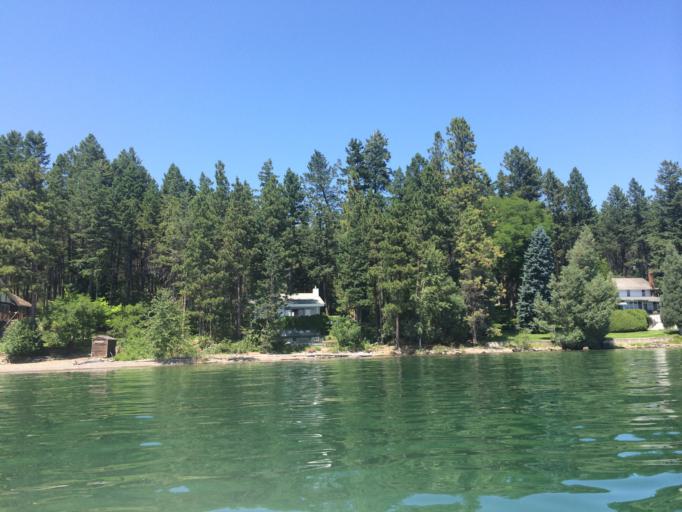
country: US
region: Montana
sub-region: Flathead County
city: Lakeside
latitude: 48.0352
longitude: -114.2225
